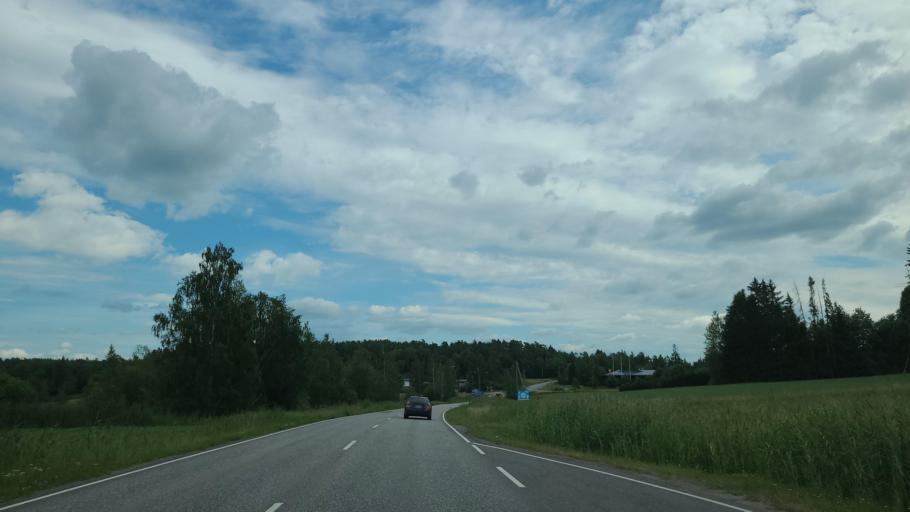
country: FI
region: Varsinais-Suomi
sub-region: Turku
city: Rymaettylae
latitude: 60.3794
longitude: 21.9434
